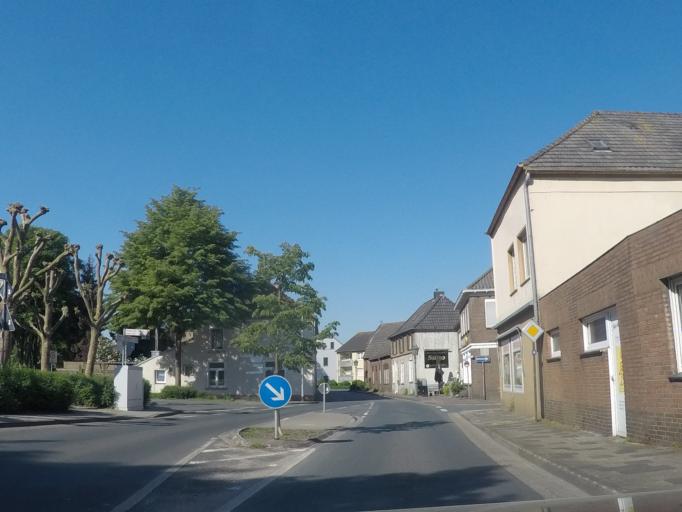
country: DE
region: North Rhine-Westphalia
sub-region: Regierungsbezirk Dusseldorf
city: Kleve
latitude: 51.8734
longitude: 6.1628
